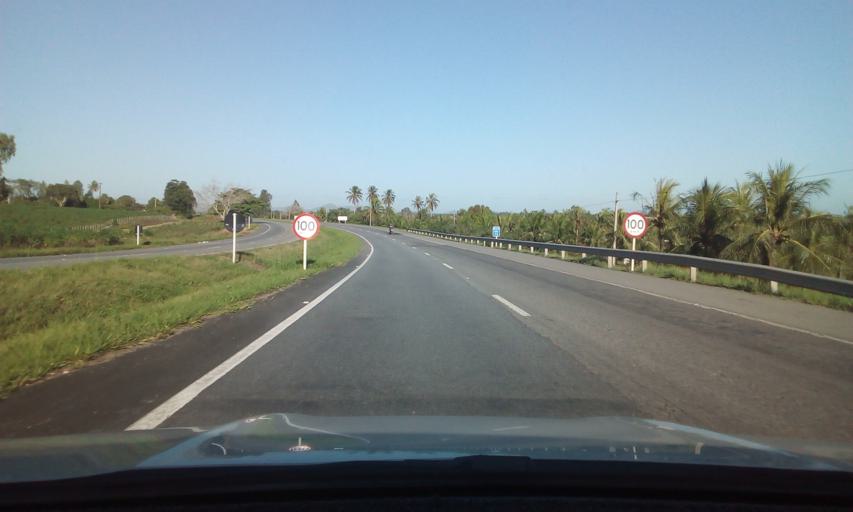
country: BR
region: Paraiba
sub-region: Pilar
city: Pilar
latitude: -7.1895
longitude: -35.2597
